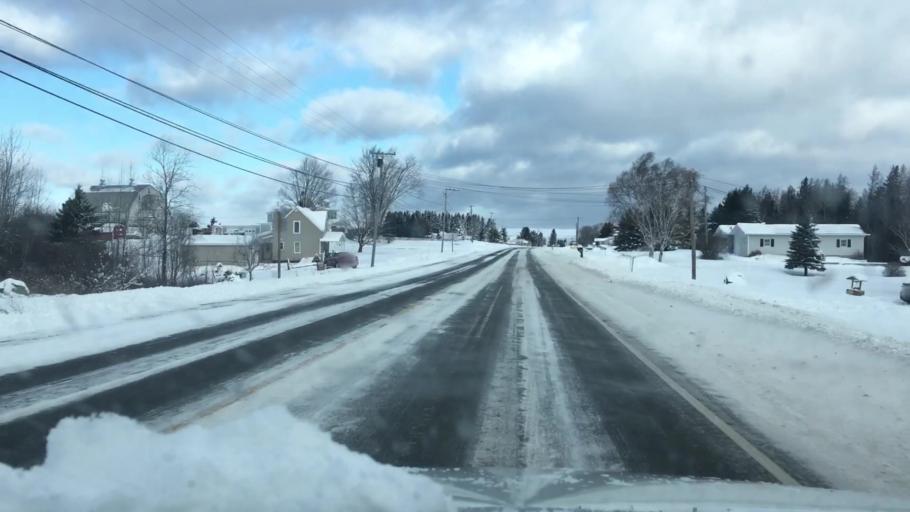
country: US
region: Maine
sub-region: Aroostook County
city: Caribou
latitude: 46.8893
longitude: -68.0146
